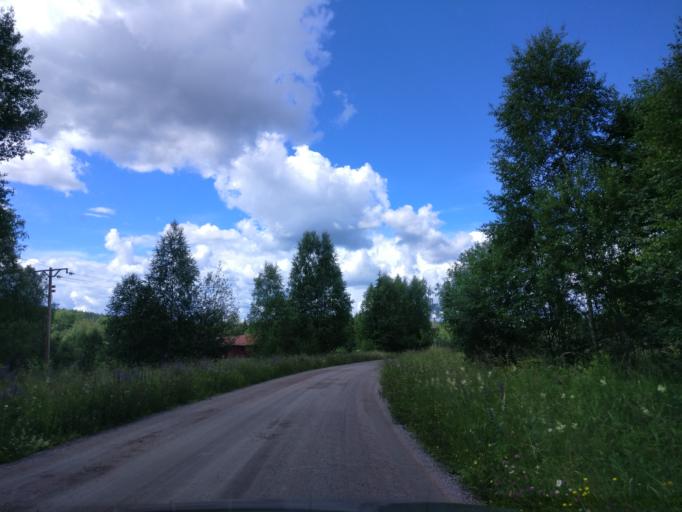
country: SE
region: Vaermland
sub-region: Hagfors Kommun
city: Hagfors
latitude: 60.0300
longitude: 13.6698
